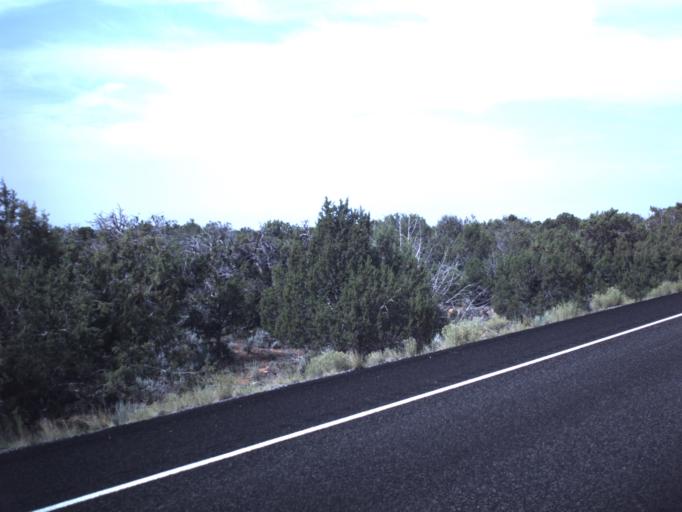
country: US
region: Utah
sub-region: Kane County
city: Kanab
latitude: 37.1791
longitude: -112.6336
